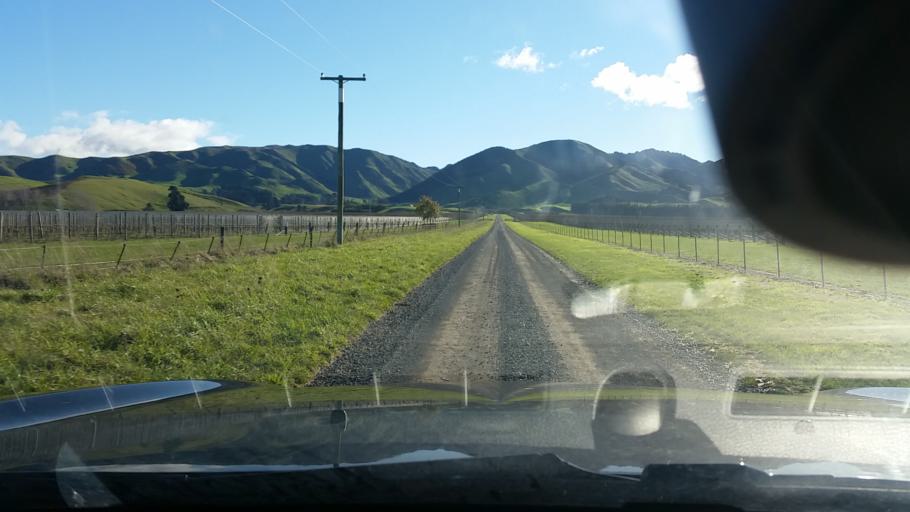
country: NZ
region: Marlborough
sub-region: Marlborough District
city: Blenheim
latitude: -41.6434
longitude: 174.0448
